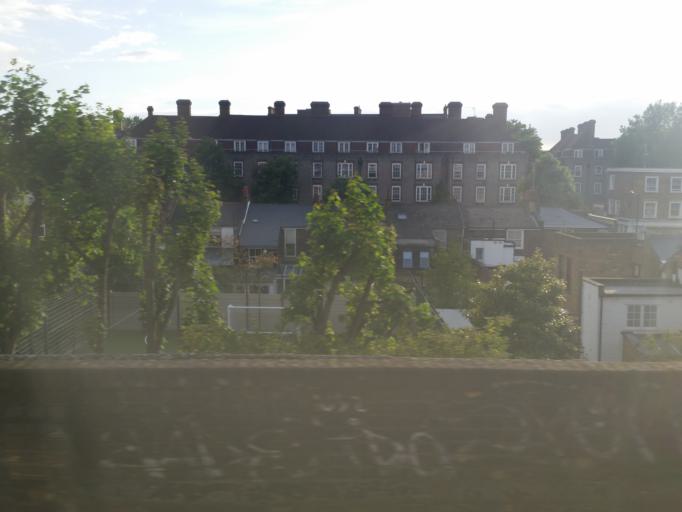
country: GB
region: England
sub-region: Greater London
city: Camden Town
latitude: 51.5447
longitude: -0.1463
